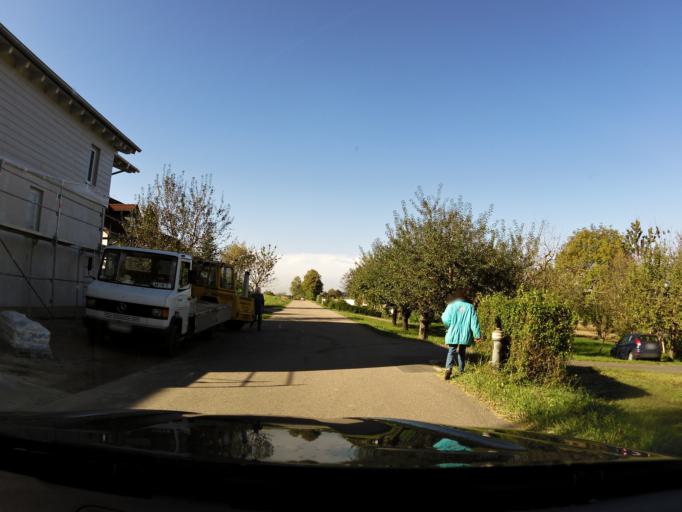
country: DE
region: Bavaria
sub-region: Lower Bavaria
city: Vilsheim
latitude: 48.4296
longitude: 12.1378
